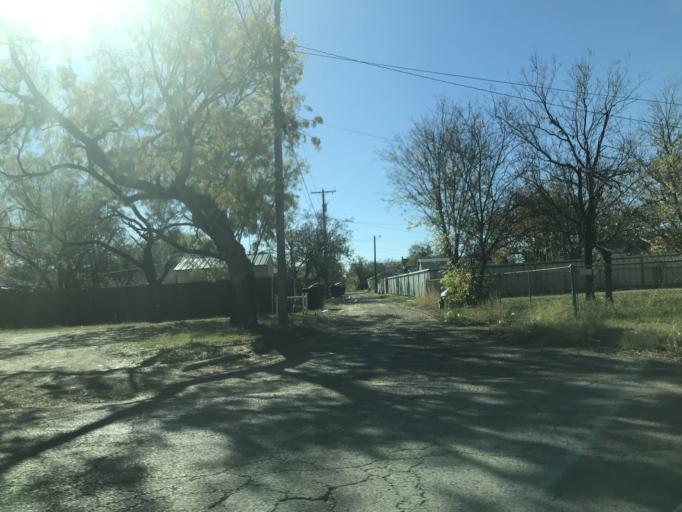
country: US
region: Texas
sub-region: Taylor County
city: Abilene
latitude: 32.4641
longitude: -99.7371
